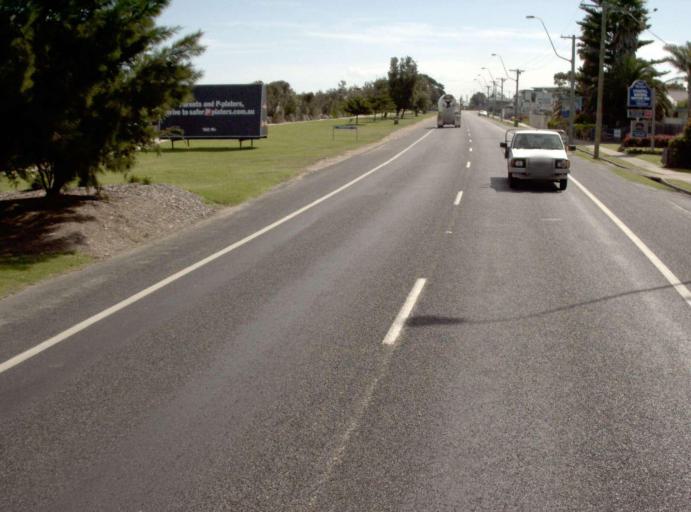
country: AU
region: Victoria
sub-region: East Gippsland
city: Lakes Entrance
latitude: -37.8776
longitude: 147.9990
